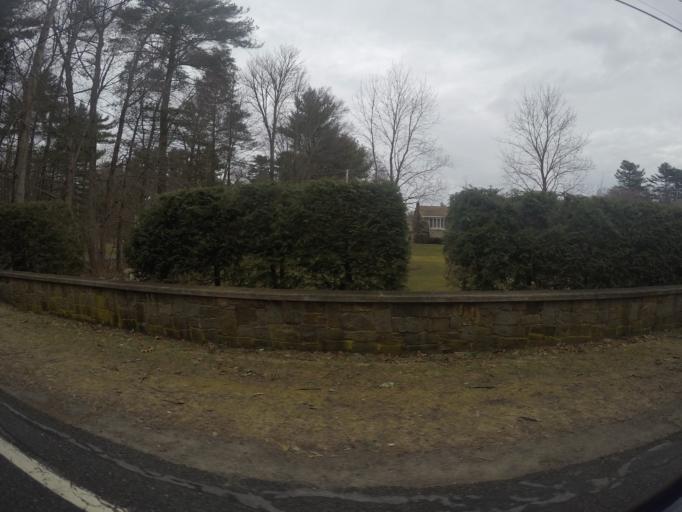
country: US
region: Massachusetts
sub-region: Bristol County
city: Easton
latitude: 42.0435
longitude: -71.1492
